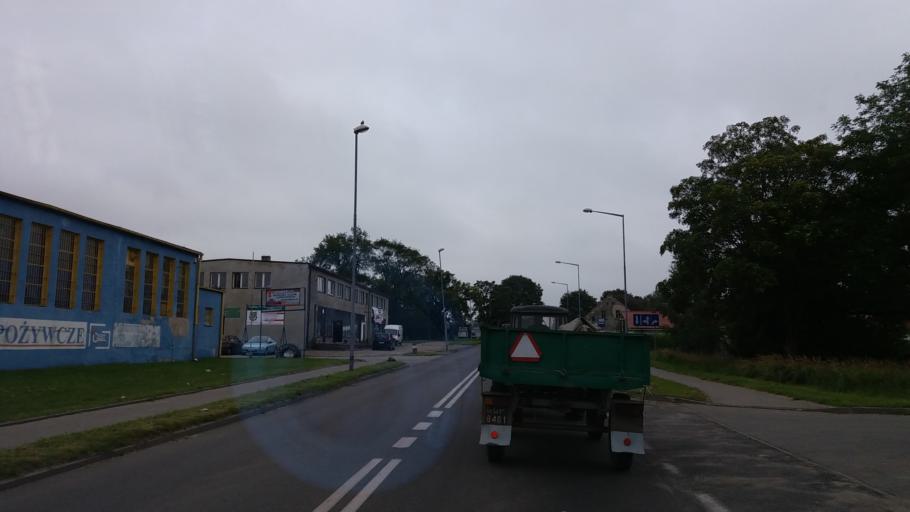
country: PL
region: West Pomeranian Voivodeship
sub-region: Powiat choszczenski
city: Choszczno
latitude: 53.1641
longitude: 15.4003
